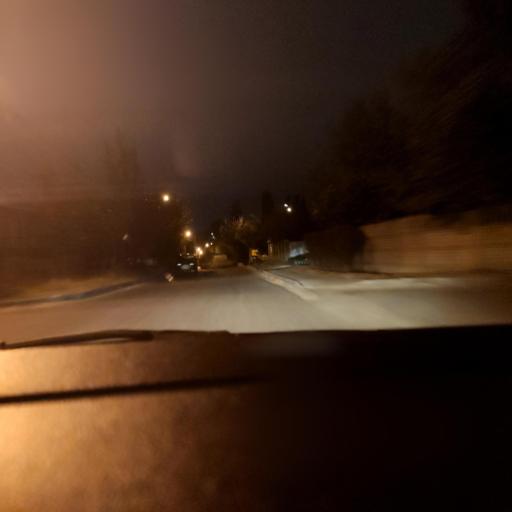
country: RU
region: Voronezj
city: Voronezh
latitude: 51.6960
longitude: 39.1747
